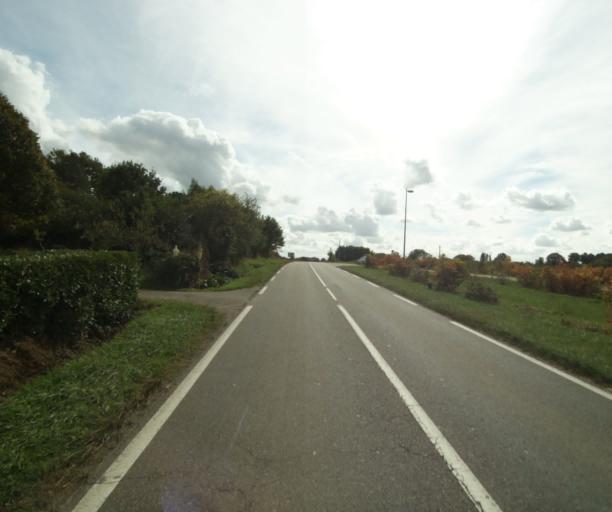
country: FR
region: Midi-Pyrenees
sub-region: Departement du Gers
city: Eauze
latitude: 43.8380
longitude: 0.0927
